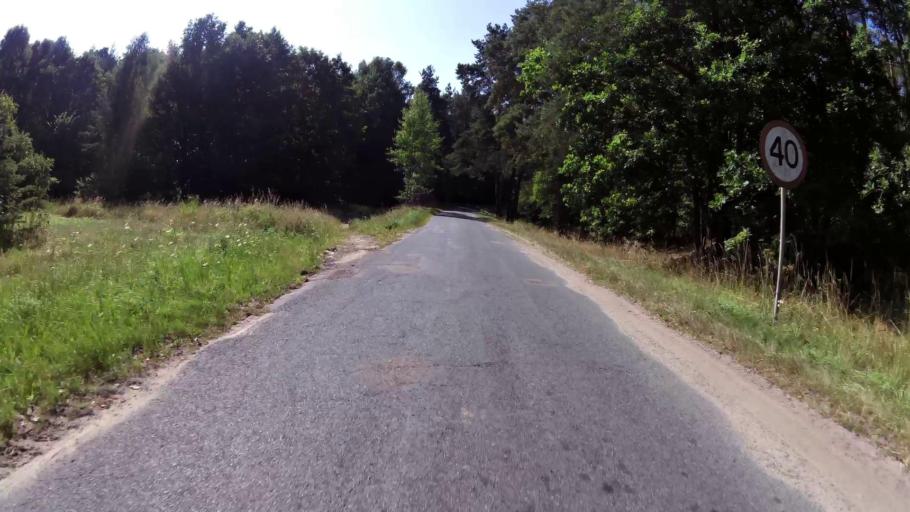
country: PL
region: West Pomeranian Voivodeship
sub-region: Powiat drawski
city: Czaplinek
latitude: 53.4321
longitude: 16.2673
